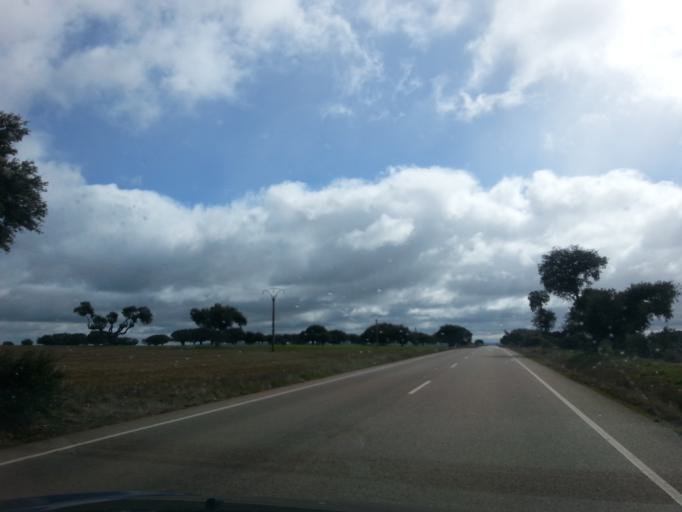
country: ES
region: Castille and Leon
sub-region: Provincia de Salamanca
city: Cabrillas
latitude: 40.7588
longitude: -6.1974
